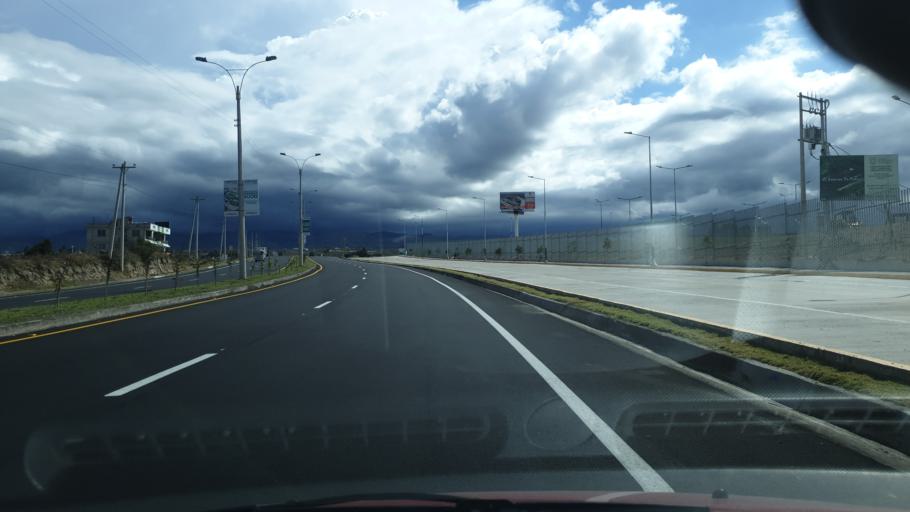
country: EC
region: Tungurahua
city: Ambato
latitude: -1.3009
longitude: -78.6339
